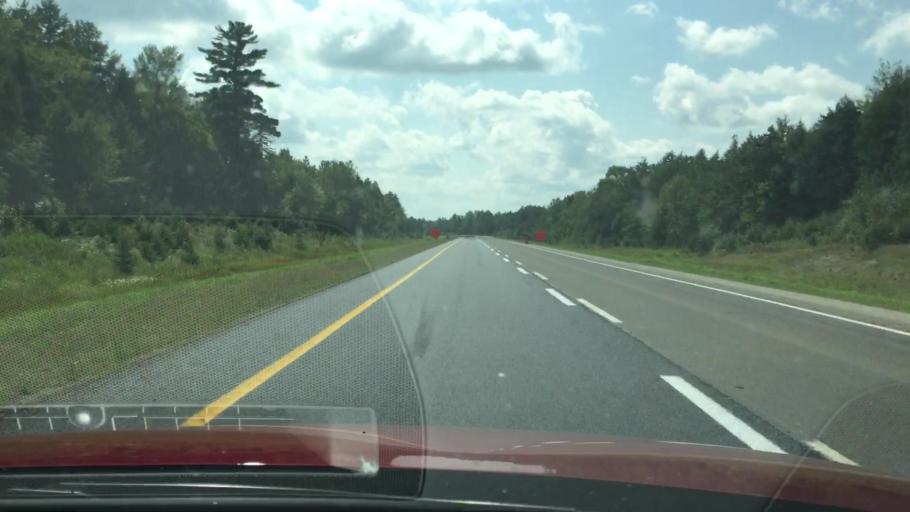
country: US
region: Maine
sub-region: Penobscot County
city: Medway
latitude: 45.7060
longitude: -68.4801
